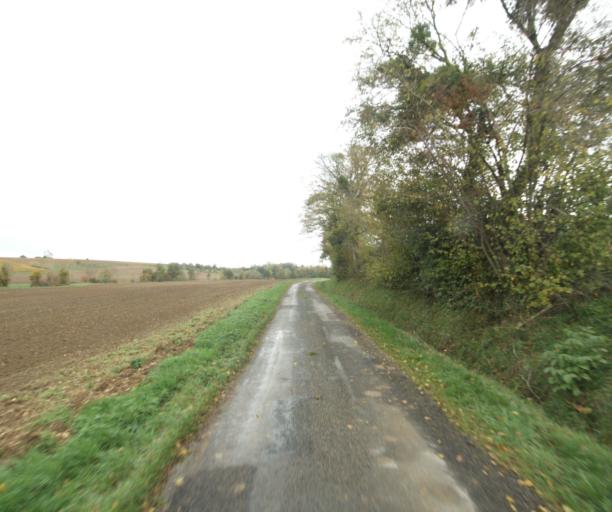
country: FR
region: Rhone-Alpes
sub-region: Departement de l'Ain
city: Pont-de-Vaux
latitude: 46.4738
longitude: 4.8616
